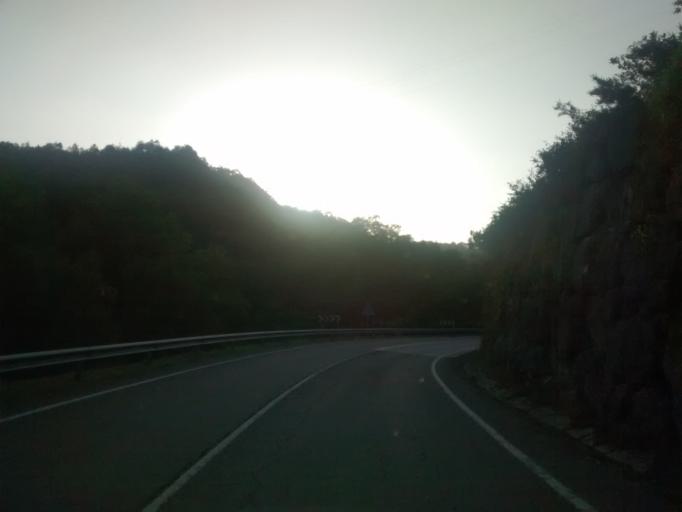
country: ES
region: Cantabria
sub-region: Provincia de Cantabria
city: Ruente
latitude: 43.1562
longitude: -4.2352
